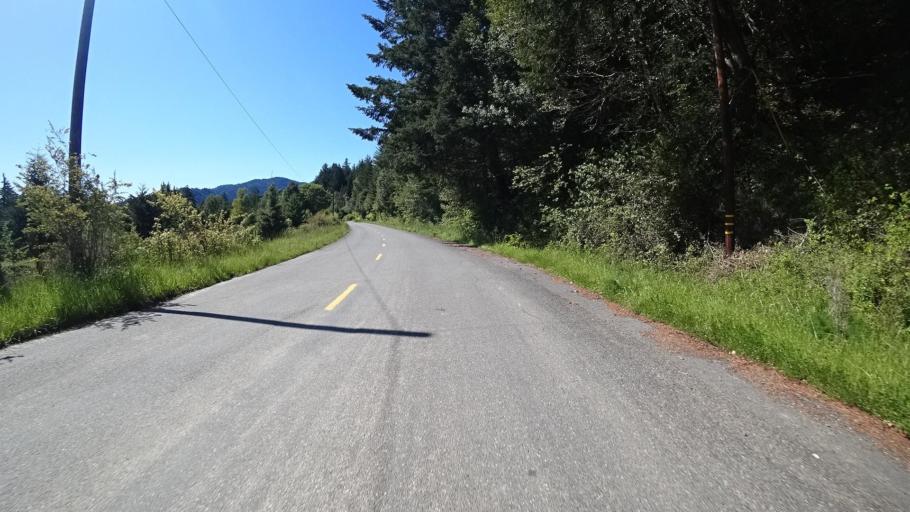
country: US
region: California
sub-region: Humboldt County
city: Rio Dell
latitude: 40.2652
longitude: -124.1971
